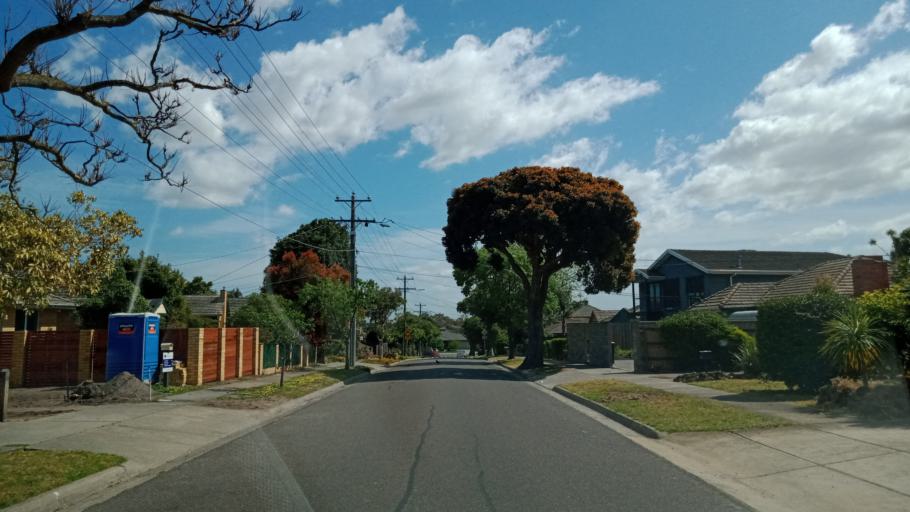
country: AU
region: Victoria
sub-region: Kingston
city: Chelsea Heights
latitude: -38.0415
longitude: 145.1351
